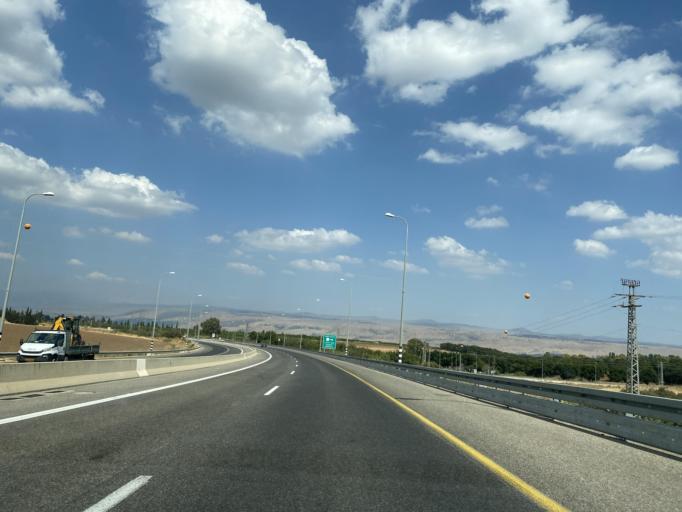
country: IL
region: Northern District
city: Rosh Pinna
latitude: 33.0293
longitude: 35.5688
